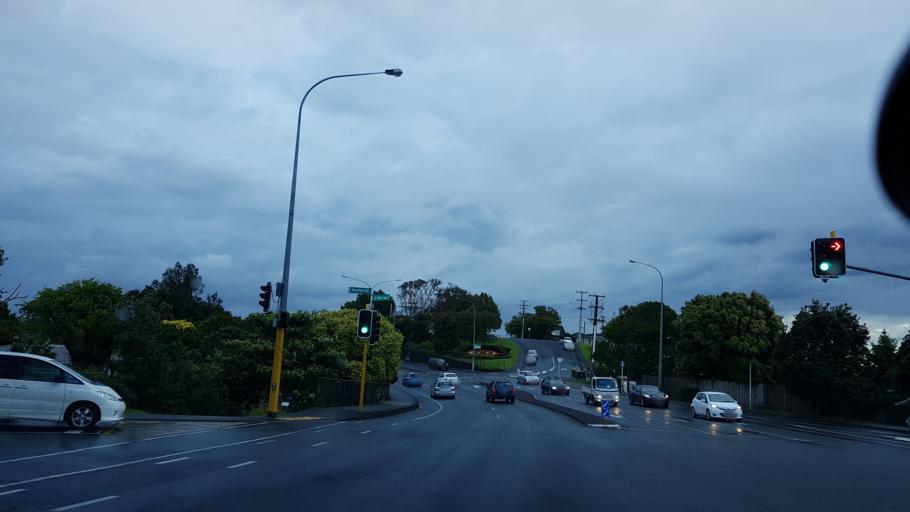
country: NZ
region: Auckland
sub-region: Auckland
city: North Shore
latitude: -36.7771
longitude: 174.7229
